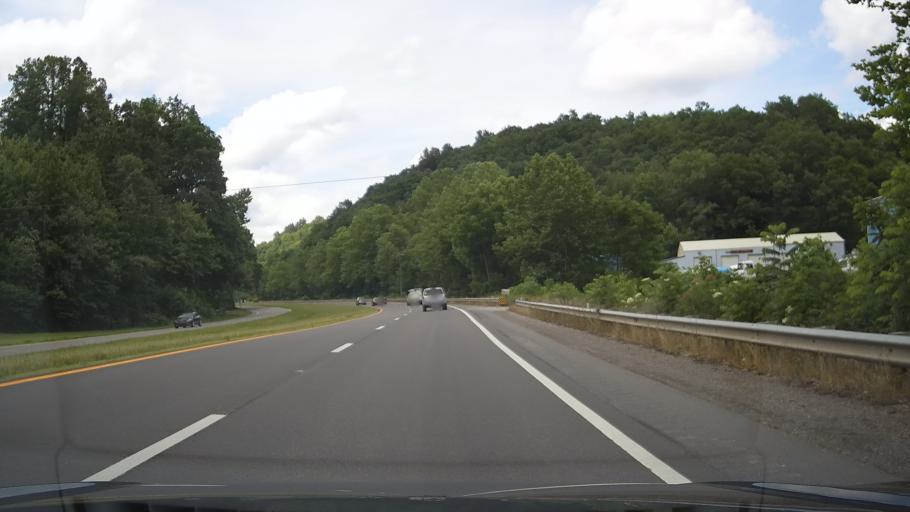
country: US
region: Virginia
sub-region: Wise County
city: Pound
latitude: 37.0721
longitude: -82.5997
